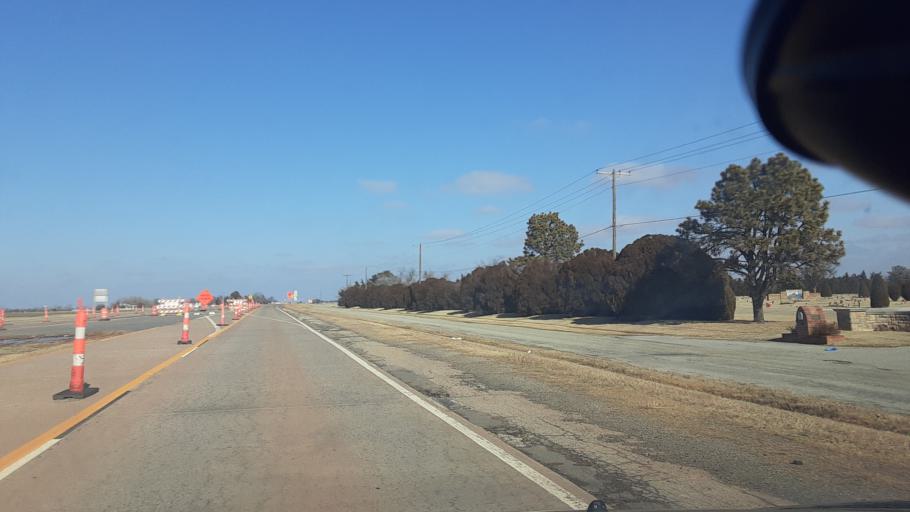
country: US
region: Oklahoma
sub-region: Garfield County
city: Enid
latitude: 36.4577
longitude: -97.8729
